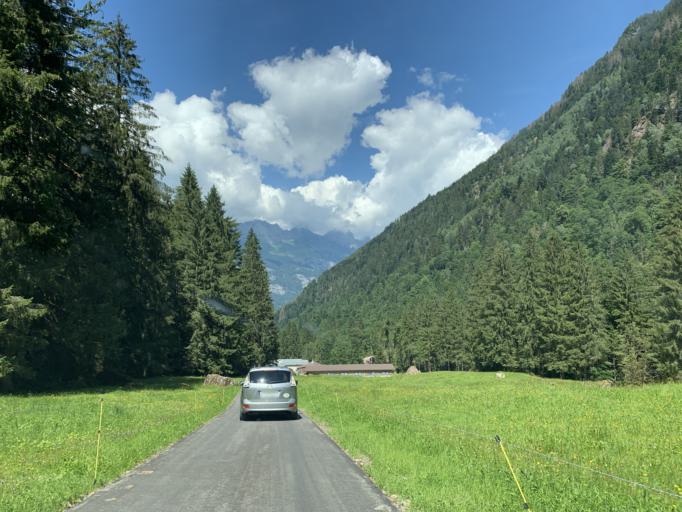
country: CH
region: Saint Gallen
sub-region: Wahlkreis Sarganserland
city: Quarten
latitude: 47.0904
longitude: 9.2059
